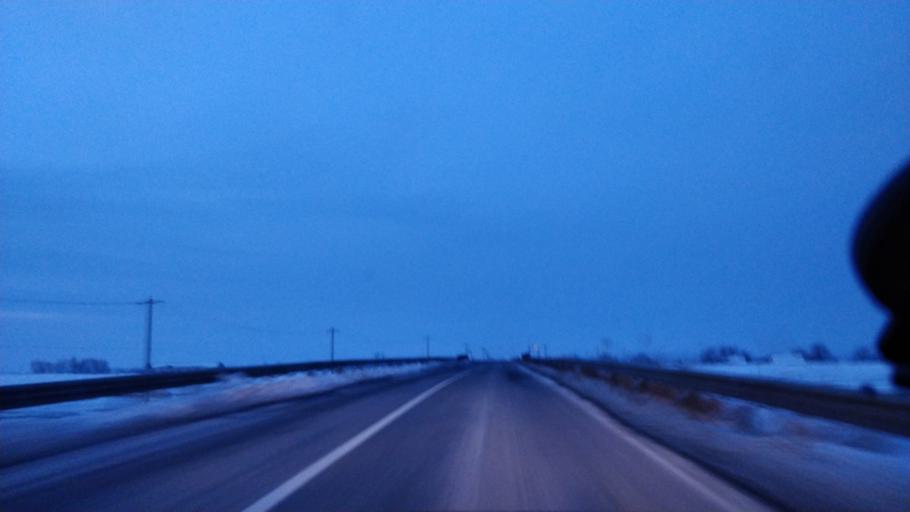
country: RO
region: Vrancea
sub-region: Comuna Nanesti
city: Nanesti
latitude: 45.5741
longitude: 27.4980
